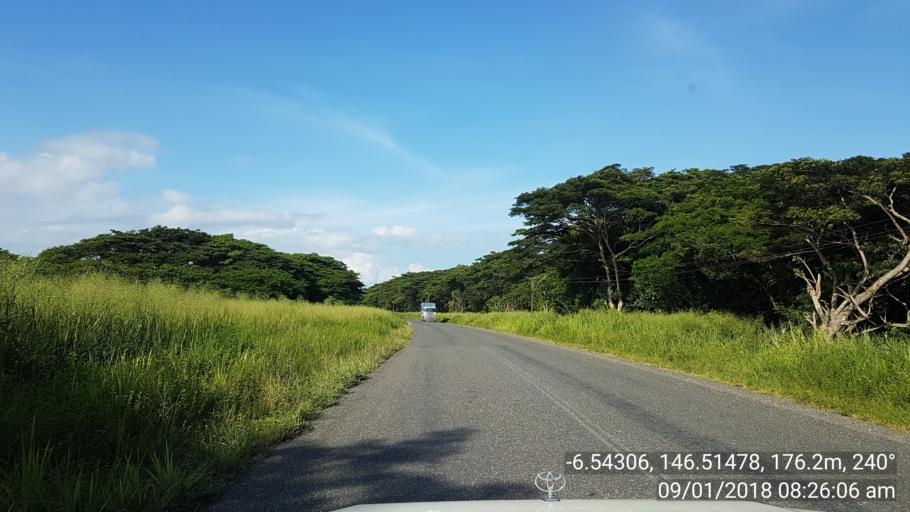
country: PG
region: Morobe
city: Lae
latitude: -6.5430
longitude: 146.5149
